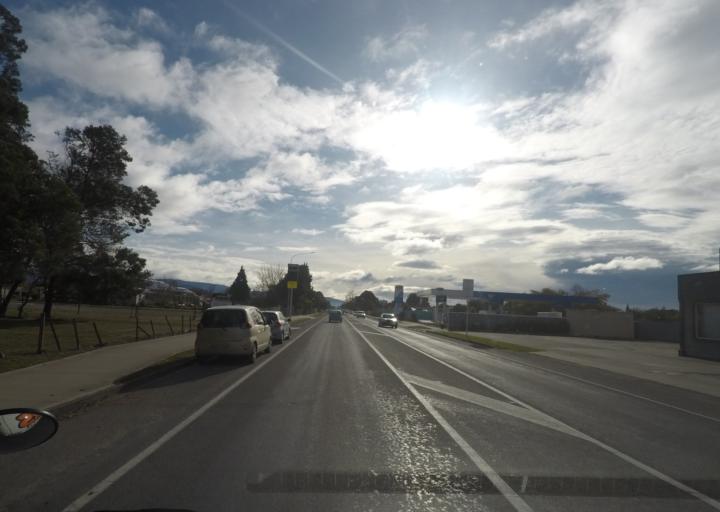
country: NZ
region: Tasman
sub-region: Tasman District
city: Motueka
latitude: -41.1310
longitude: 173.0100
